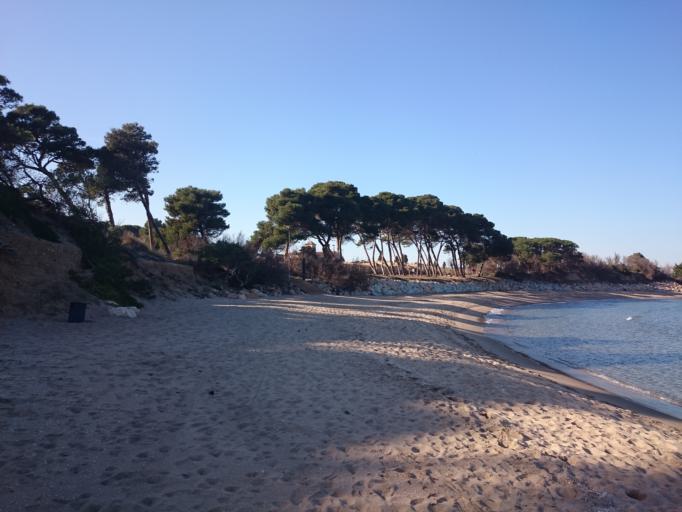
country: ES
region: Catalonia
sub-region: Provincia de Girona
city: l'Escala
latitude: 42.1333
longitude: 3.1224
